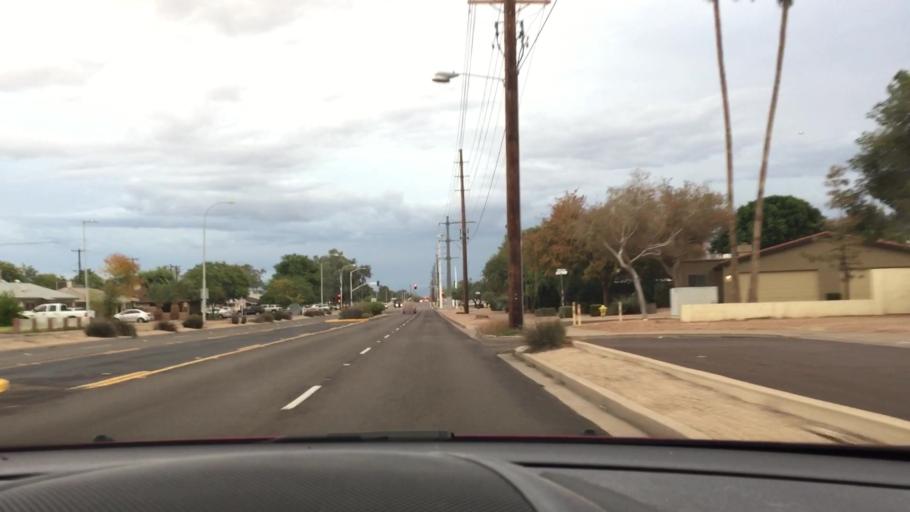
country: US
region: Arizona
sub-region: Maricopa County
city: Tempe
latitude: 33.4512
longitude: -111.9204
